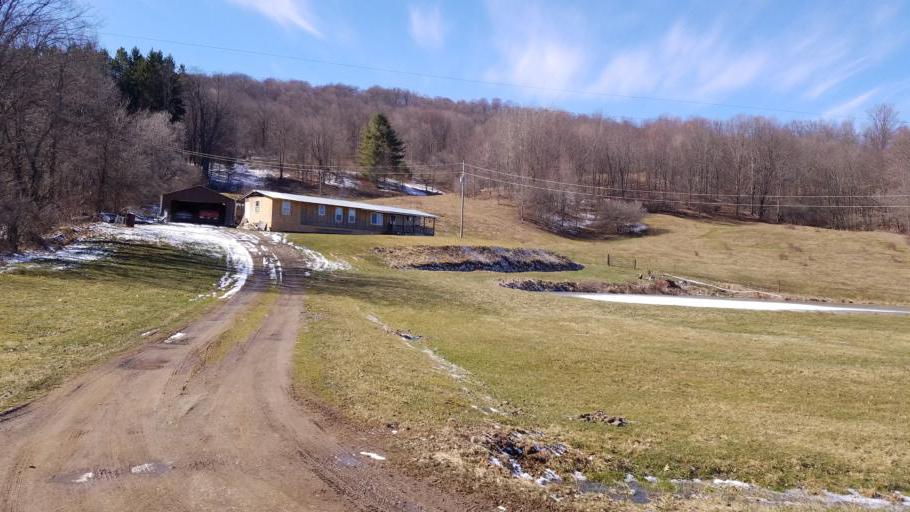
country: US
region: New York
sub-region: Allegany County
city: Wellsville
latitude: 42.0638
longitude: -77.9295
